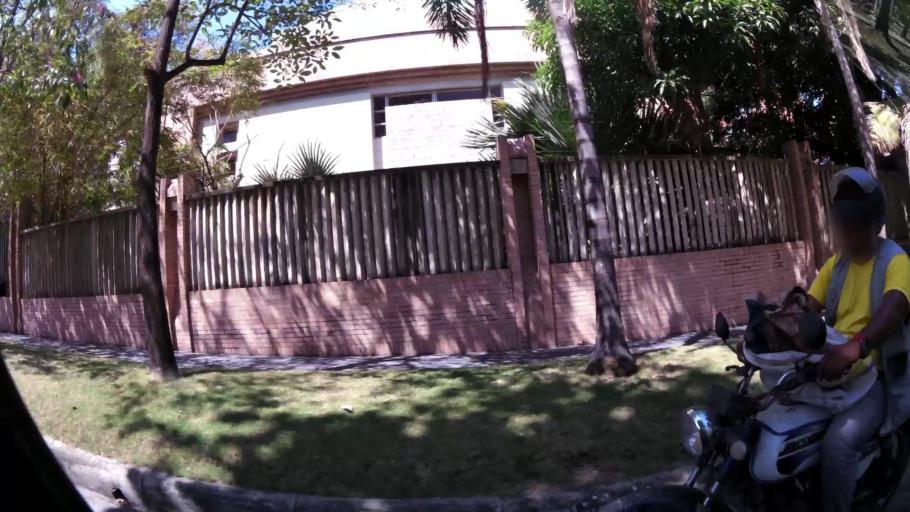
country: CO
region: Atlantico
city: Barranquilla
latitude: 11.0106
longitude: -74.8085
